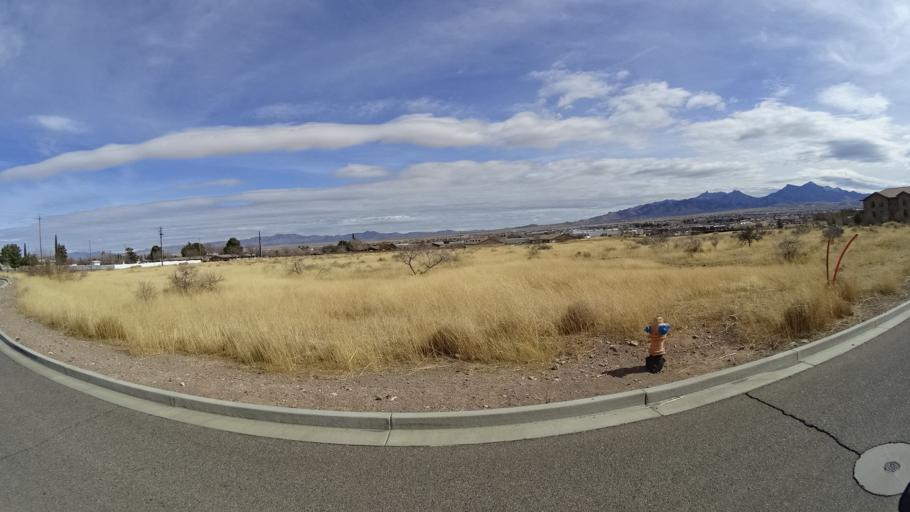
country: US
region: Arizona
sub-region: Mohave County
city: New Kingman-Butler
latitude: 35.2289
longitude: -114.0426
